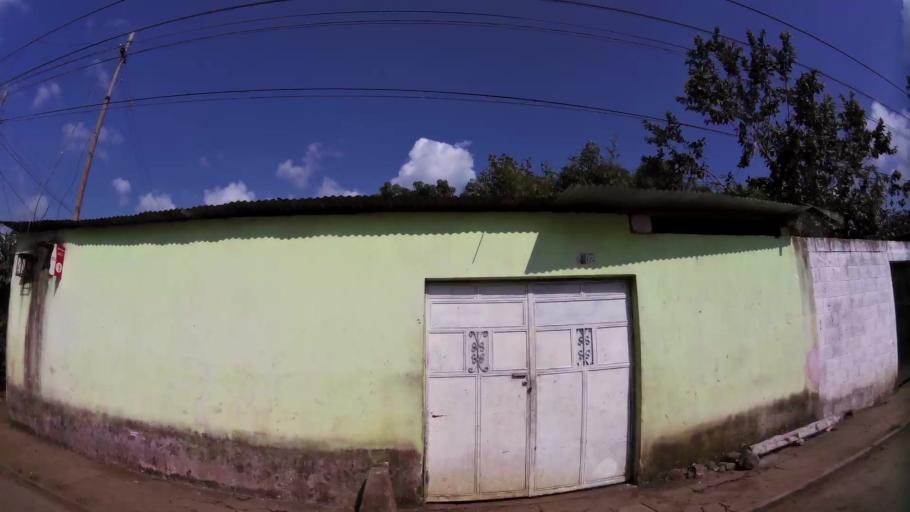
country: GT
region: Retalhuleu
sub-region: Municipio de Retalhuleu
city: Retalhuleu
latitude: 14.5428
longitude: -91.6802
